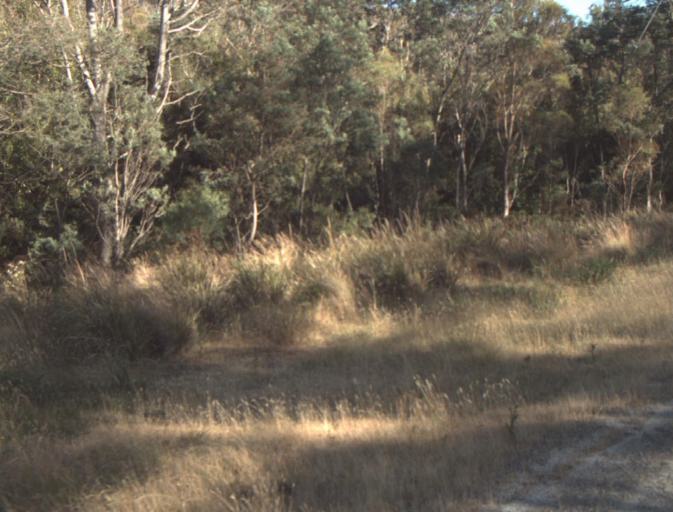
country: AU
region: Tasmania
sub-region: Launceston
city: Newstead
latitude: -41.4220
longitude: 147.2559
